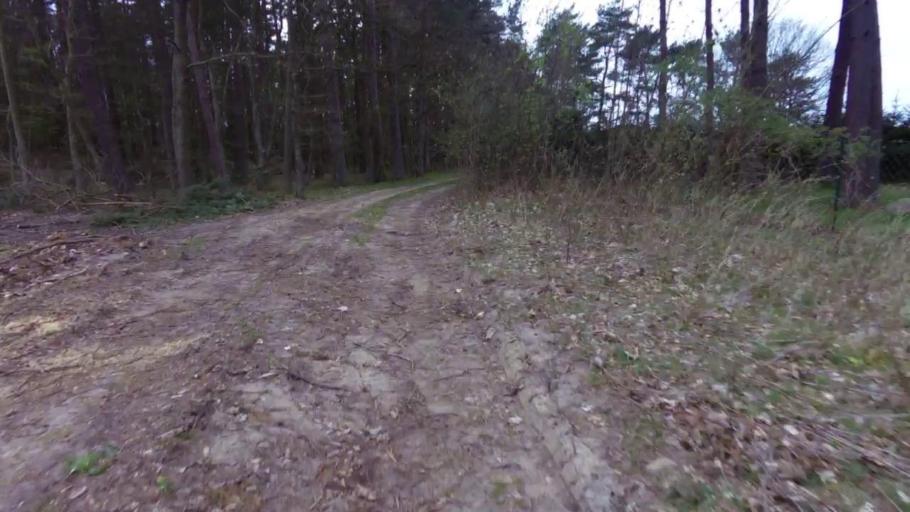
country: PL
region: West Pomeranian Voivodeship
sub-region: Powiat kamienski
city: Wolin
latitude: 53.9630
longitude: 14.5809
